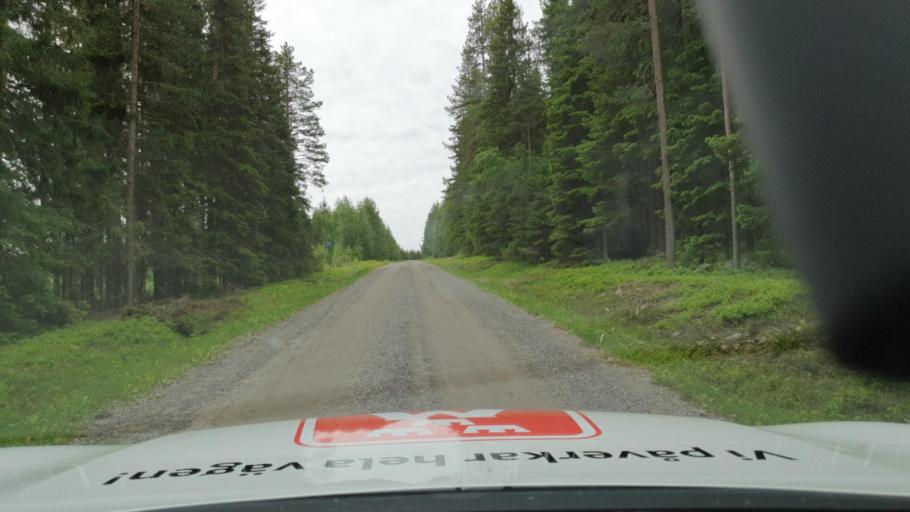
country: SE
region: Vaesterbotten
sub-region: Skelleftea Kommun
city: Burtraesk
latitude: 64.4478
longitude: 20.3848
